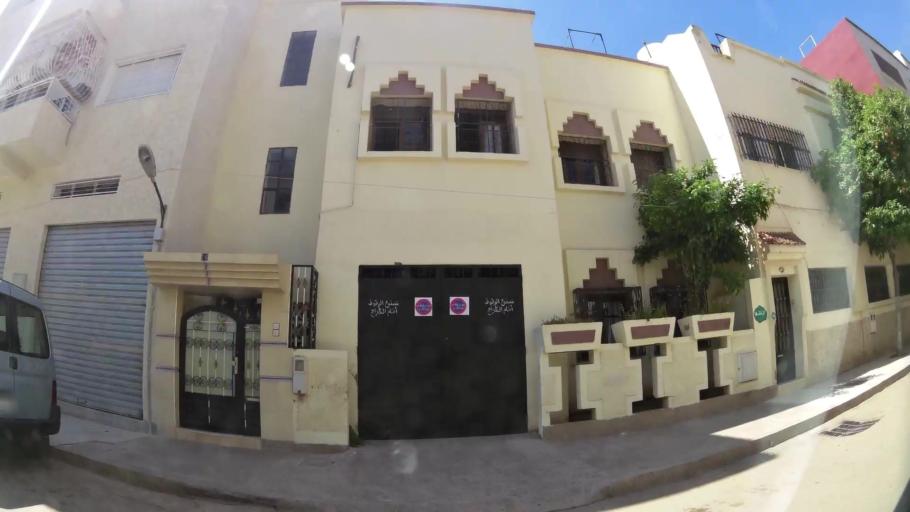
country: MA
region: Fes-Boulemane
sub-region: Fes
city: Fes
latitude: 34.0210
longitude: -5.0270
